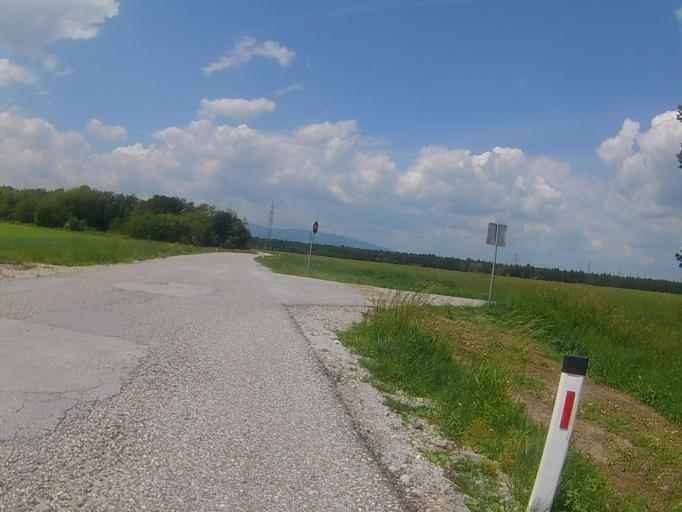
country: SI
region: Kidricevo
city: Kidricevo
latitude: 46.4253
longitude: 15.7810
